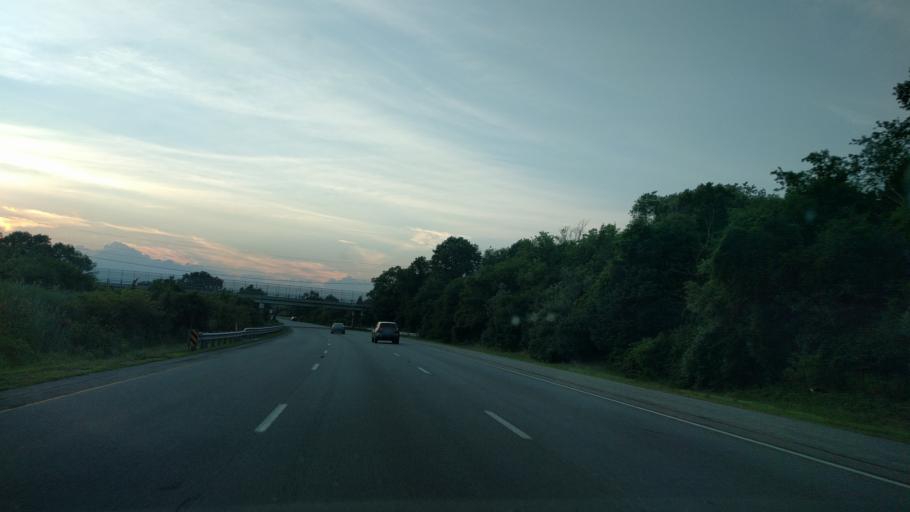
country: US
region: Massachusetts
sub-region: Bristol County
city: Swansea
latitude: 41.7277
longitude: -71.1869
